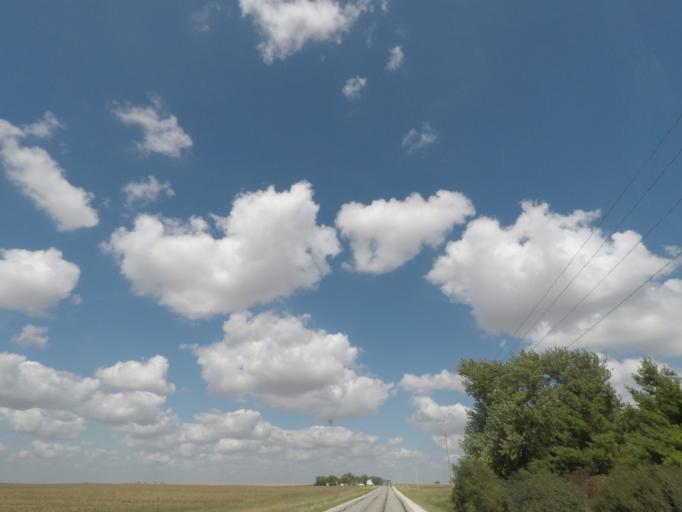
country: US
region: Iowa
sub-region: Story County
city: Nevada
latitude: 42.0635
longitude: -93.4056
